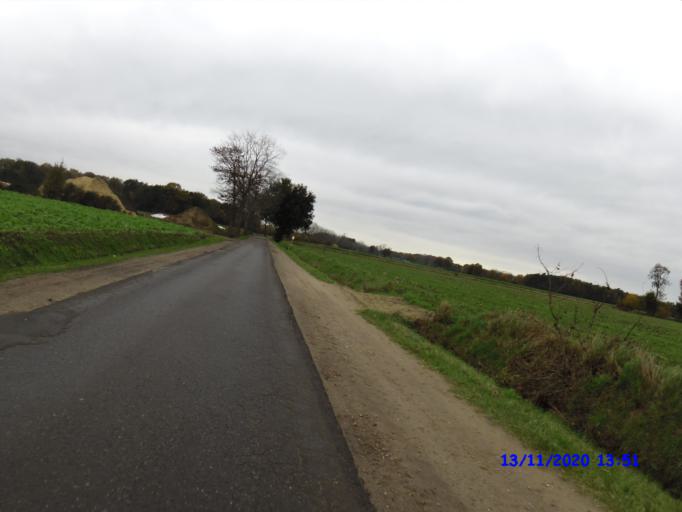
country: BE
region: Flanders
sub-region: Provincie Antwerpen
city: Kasterlee
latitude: 51.2786
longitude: 4.9710
